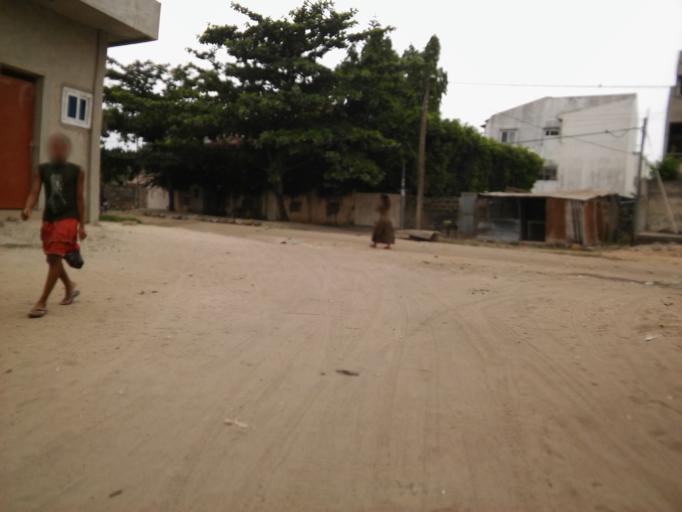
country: BJ
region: Littoral
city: Cotonou
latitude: 6.3918
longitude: 2.3722
